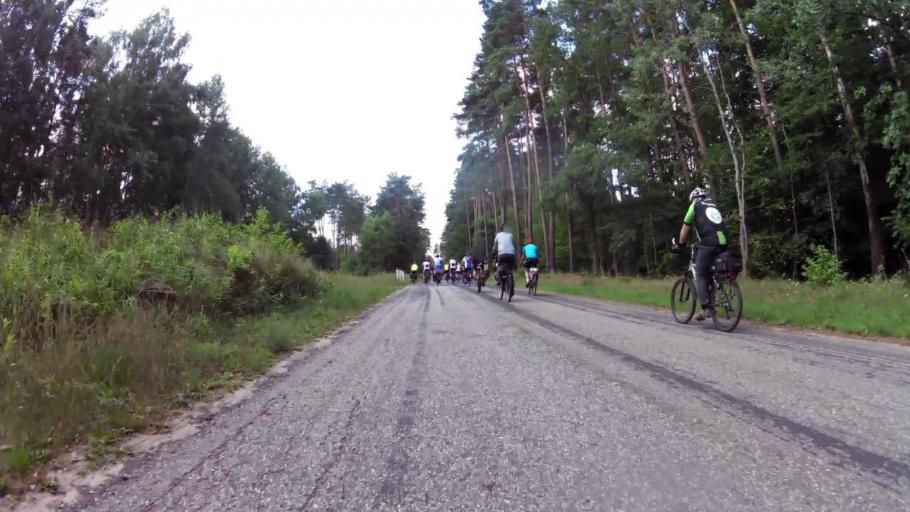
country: PL
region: West Pomeranian Voivodeship
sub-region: Powiat drawski
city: Drawsko Pomorskie
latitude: 53.4674
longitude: 15.7813
